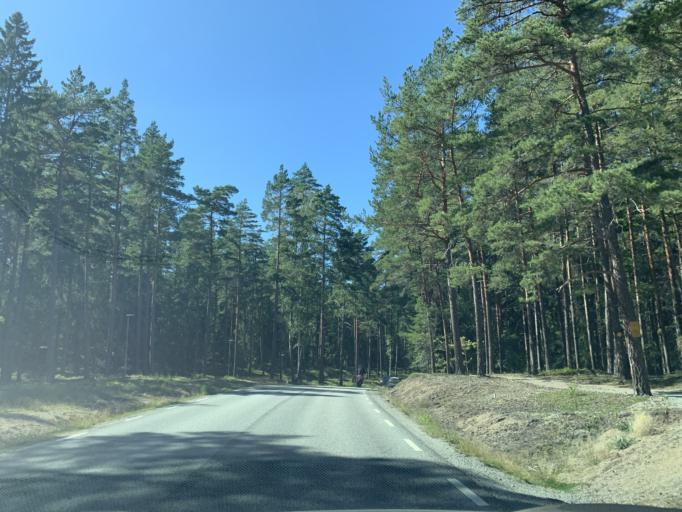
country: SE
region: Stockholm
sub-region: Ekero Kommun
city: Ekeroe
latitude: 59.2723
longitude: 17.8353
